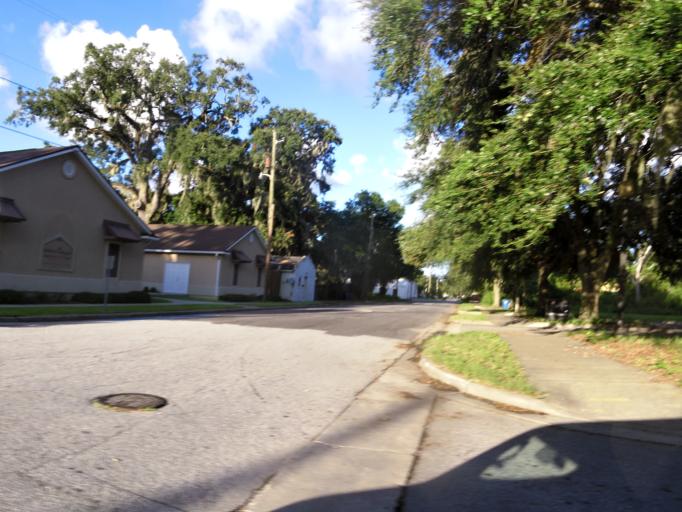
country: US
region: Georgia
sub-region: Glynn County
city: Brunswick
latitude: 31.1551
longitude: -81.4946
